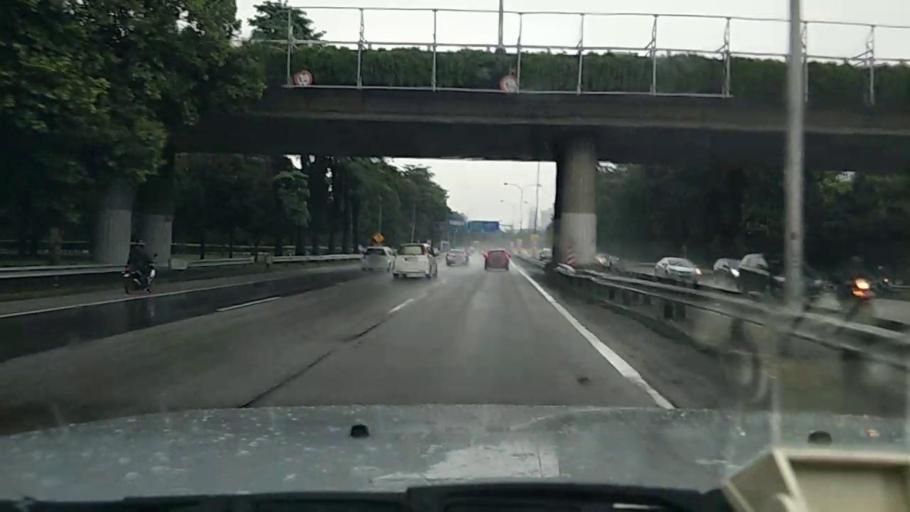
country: MY
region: Kuala Lumpur
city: Kuala Lumpur
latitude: 3.1003
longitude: 101.6990
